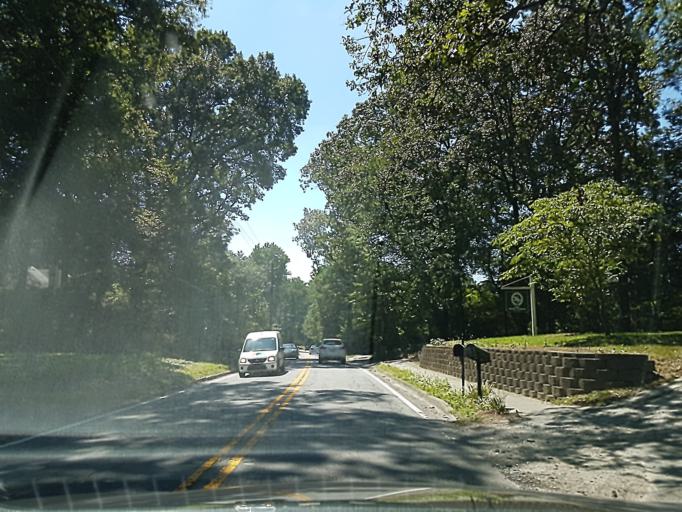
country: US
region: Georgia
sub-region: DeKalb County
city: North Druid Hills
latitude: 33.8106
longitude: -84.3206
